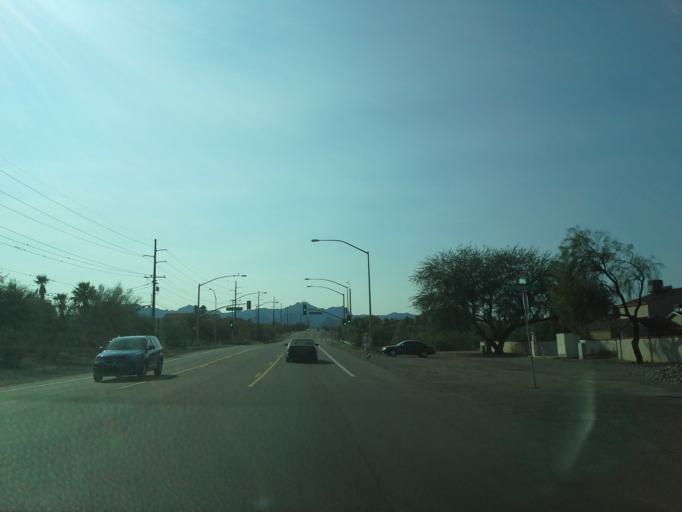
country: US
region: Arizona
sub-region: Pima County
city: Flowing Wells
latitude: 32.2508
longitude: -111.0191
